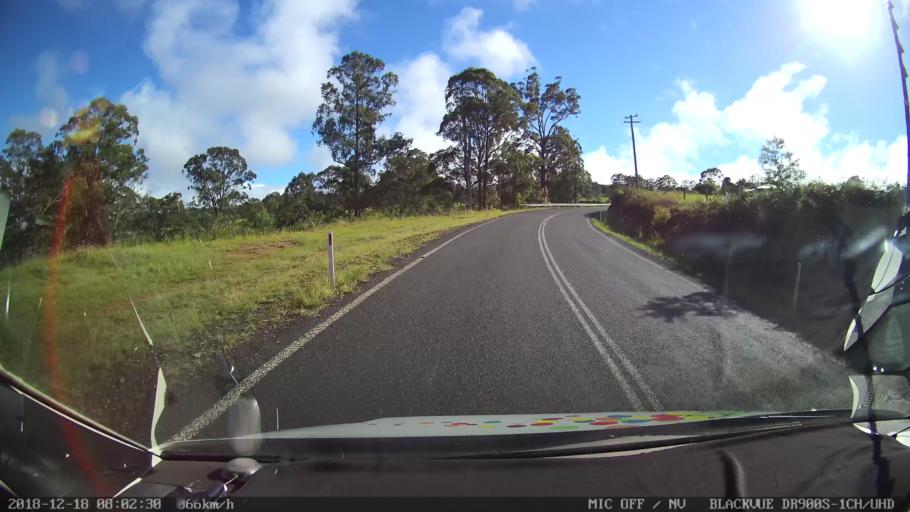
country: AU
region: New South Wales
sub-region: Kyogle
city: Kyogle
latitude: -28.3920
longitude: 152.6332
